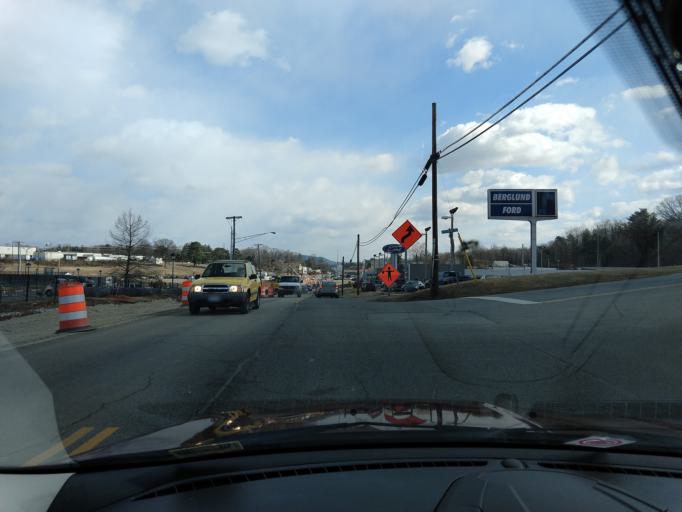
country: US
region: Virginia
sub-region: City of Salem
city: Salem
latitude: 37.2944
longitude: -80.0476
